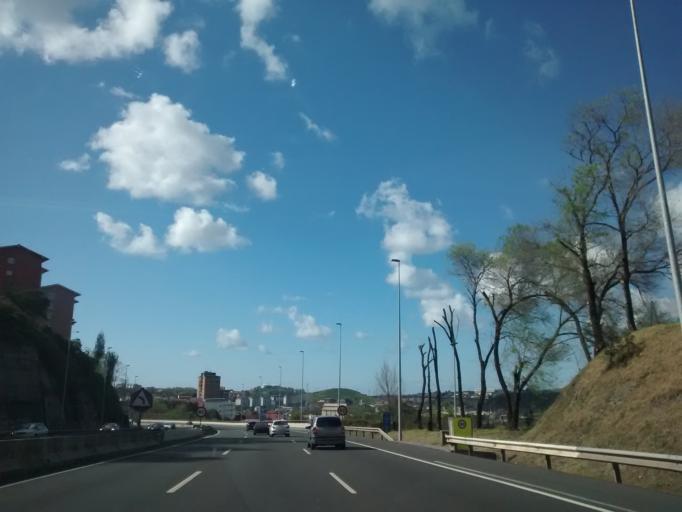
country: ES
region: Basque Country
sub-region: Bizkaia
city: Alonsotegi
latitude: 43.2717
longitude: -2.9672
